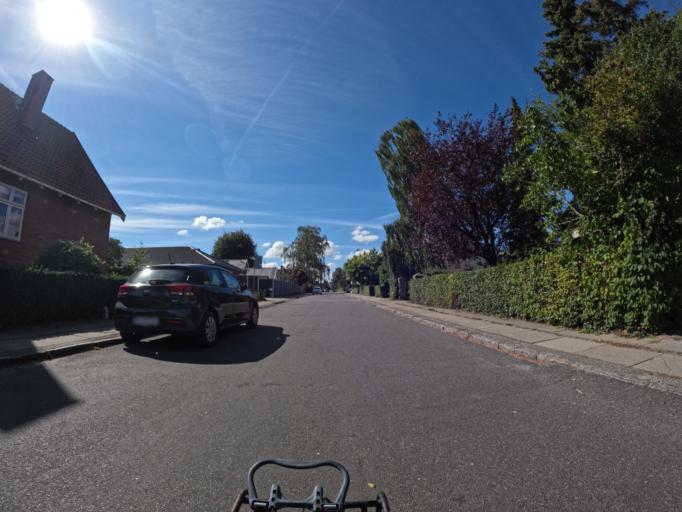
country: DK
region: Capital Region
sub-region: Hoje-Taastrup Kommune
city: Taastrup
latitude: 55.6548
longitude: 12.3137
